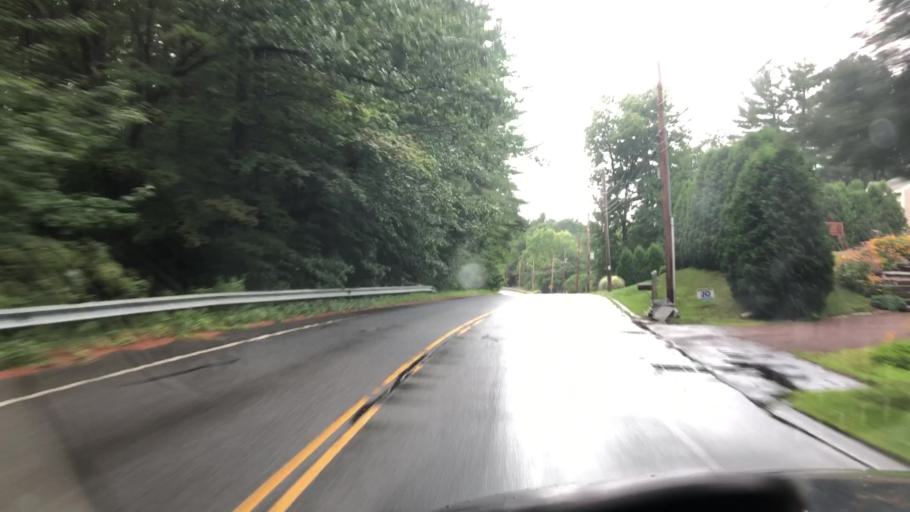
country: US
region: Massachusetts
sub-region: Hampshire County
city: Easthampton
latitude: 42.3015
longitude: -72.6817
